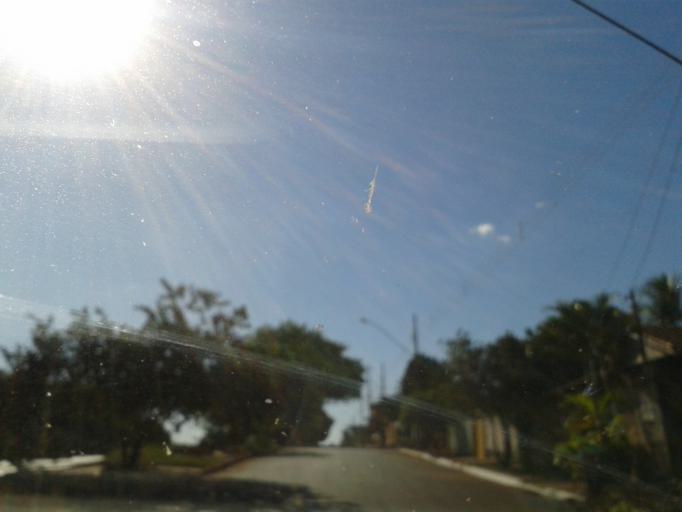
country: BR
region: Goias
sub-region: Itumbiara
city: Itumbiara
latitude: -18.4362
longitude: -49.1898
